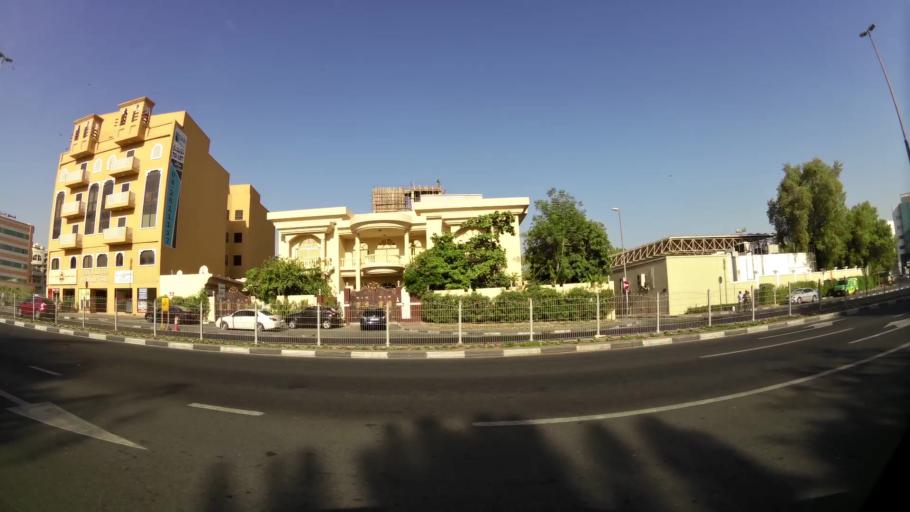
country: AE
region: Ash Shariqah
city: Sharjah
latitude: 25.2756
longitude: 55.3156
